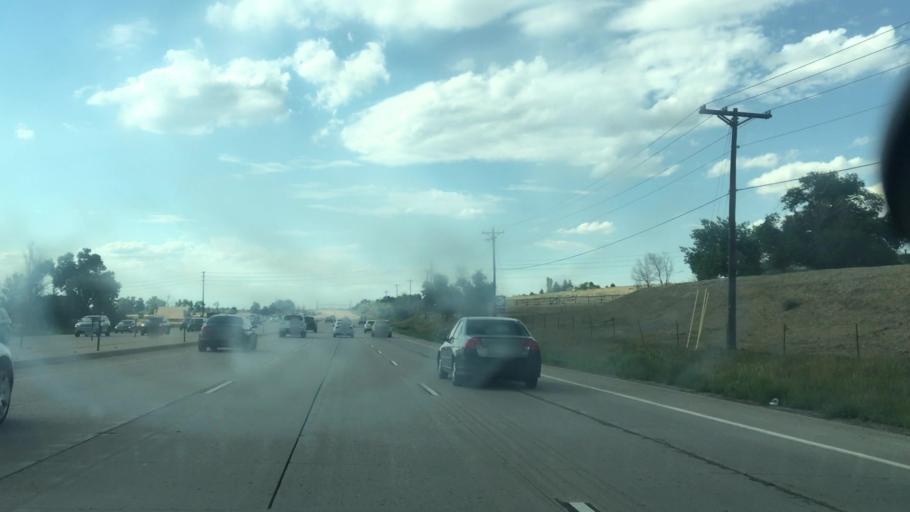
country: US
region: Colorado
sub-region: Douglas County
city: Stonegate
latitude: 39.5640
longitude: -104.7837
